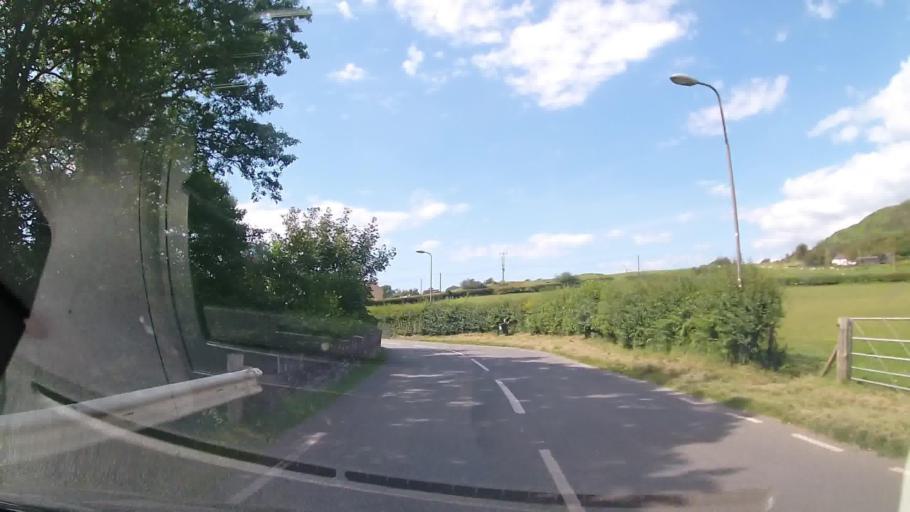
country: GB
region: Wales
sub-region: Gwynedd
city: Tywyn
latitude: 52.6088
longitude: -4.0490
